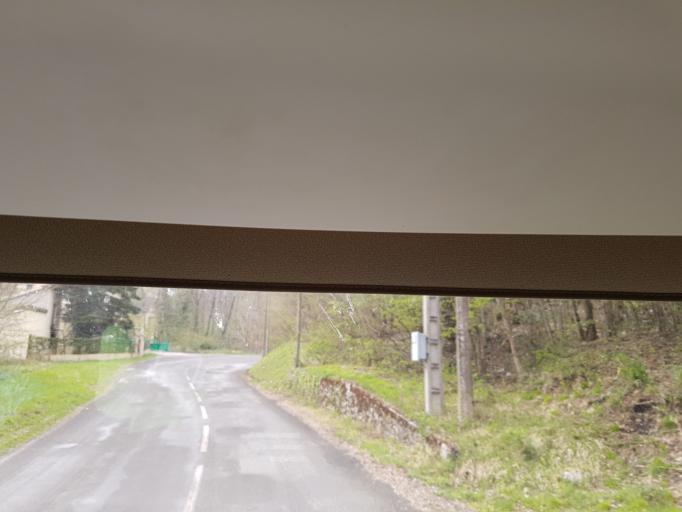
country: FR
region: Languedoc-Roussillon
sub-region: Departement de l'Aude
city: Quillan
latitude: 42.7734
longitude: 2.1678
